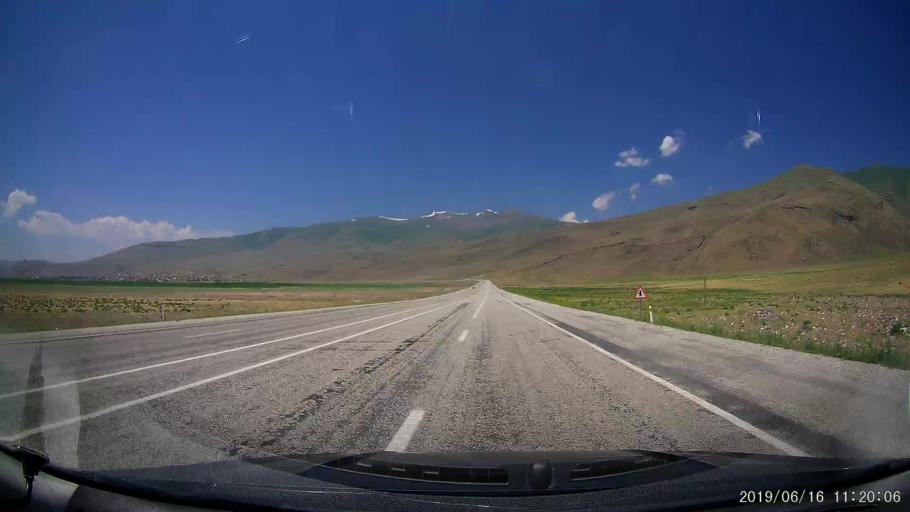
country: TR
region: Agri
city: Dogubayazit
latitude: 39.6971
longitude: 44.0991
